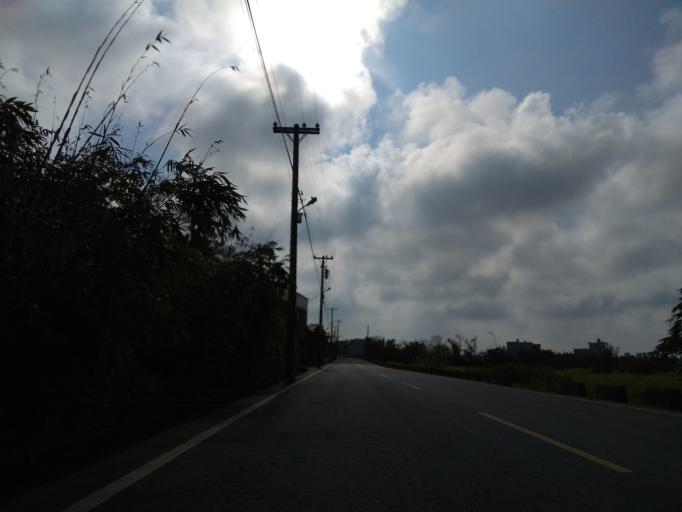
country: TW
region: Taiwan
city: Taoyuan City
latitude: 25.0604
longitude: 121.1530
